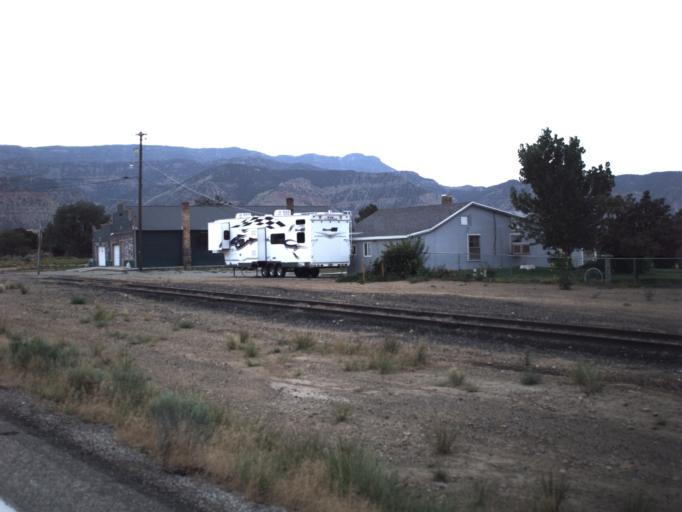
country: US
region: Utah
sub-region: Carbon County
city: East Carbon City
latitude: 39.5416
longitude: -110.4241
